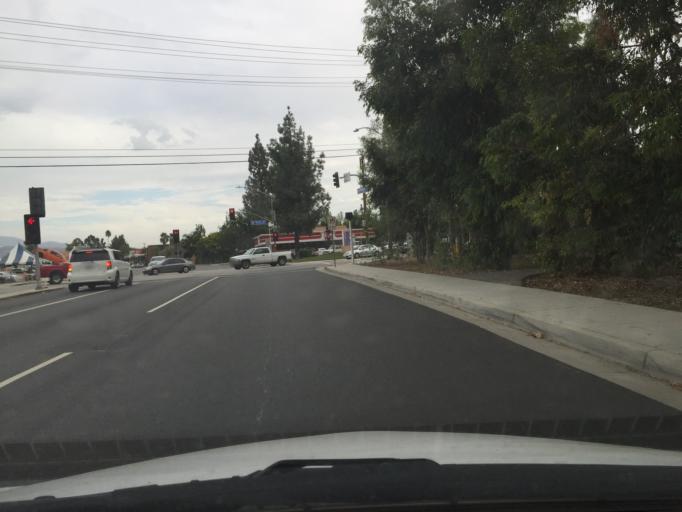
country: US
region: California
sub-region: San Bernardino County
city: Redlands
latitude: 34.0579
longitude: -117.1919
